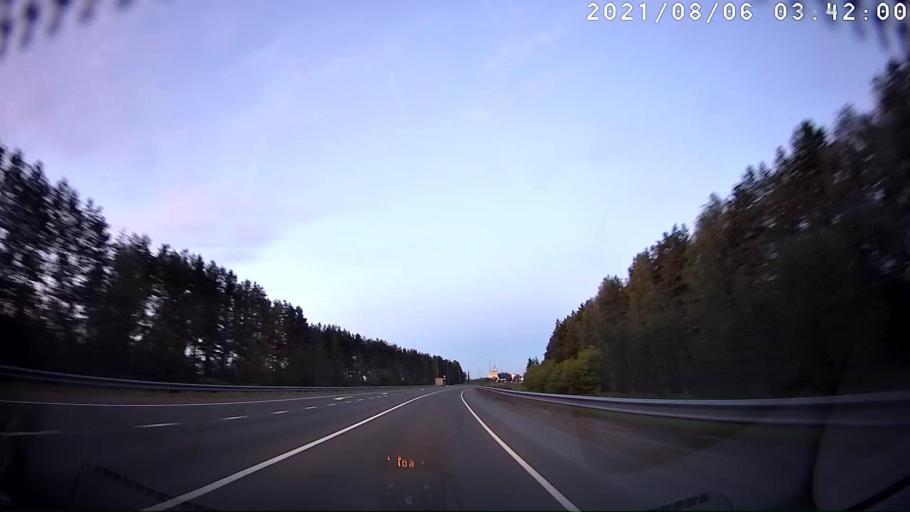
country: RU
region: Mariy-El
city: Pomary
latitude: 55.9233
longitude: 48.3745
